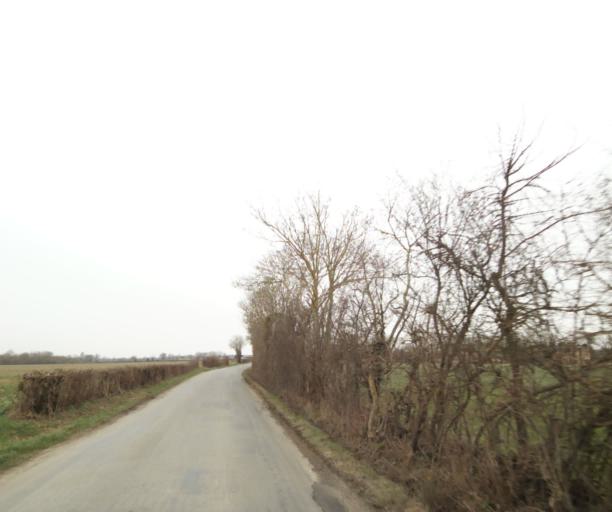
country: FR
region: Poitou-Charentes
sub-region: Departement des Deux-Sevres
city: Bessines
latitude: 46.2959
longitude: -0.4840
